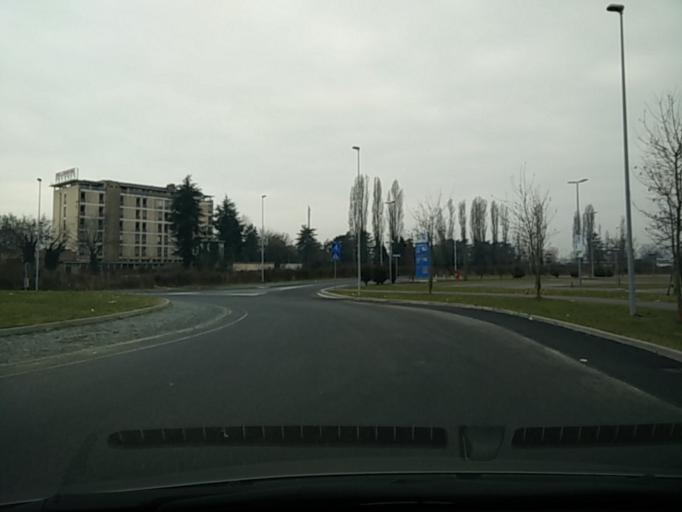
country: IT
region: Piedmont
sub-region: Provincia di Torino
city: Settimo Torinese
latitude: 45.1370
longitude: 7.7328
